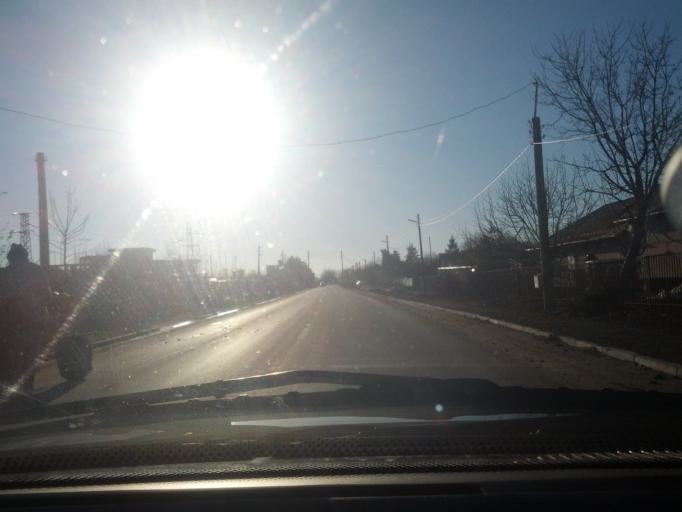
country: BG
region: Vratsa
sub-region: Obshtina Miziya
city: Miziya
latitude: 43.6539
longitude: 23.7654
